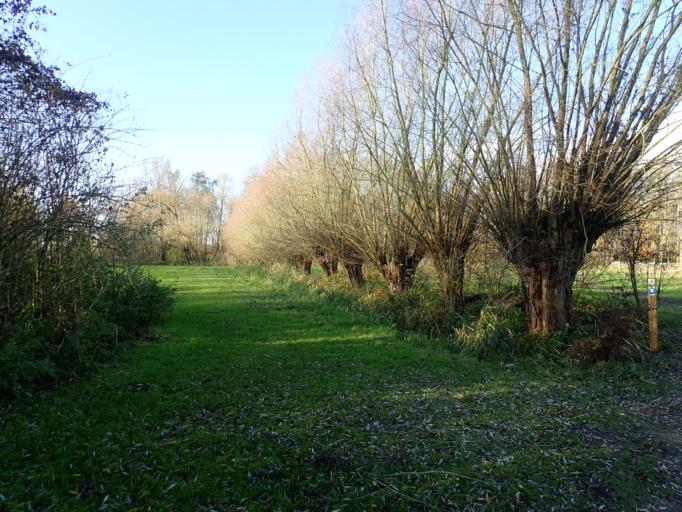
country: BE
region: Flanders
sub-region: Provincie Antwerpen
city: Boom
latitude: 51.0677
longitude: 4.3904
